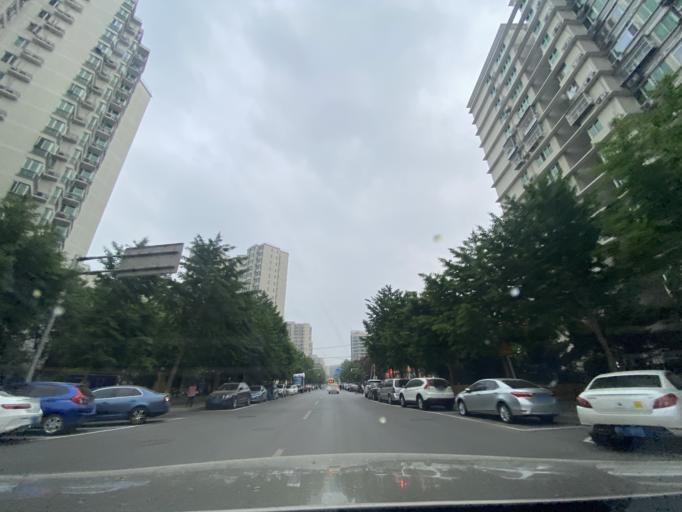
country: CN
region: Beijing
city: Sijiqing
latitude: 39.9597
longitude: 116.2743
